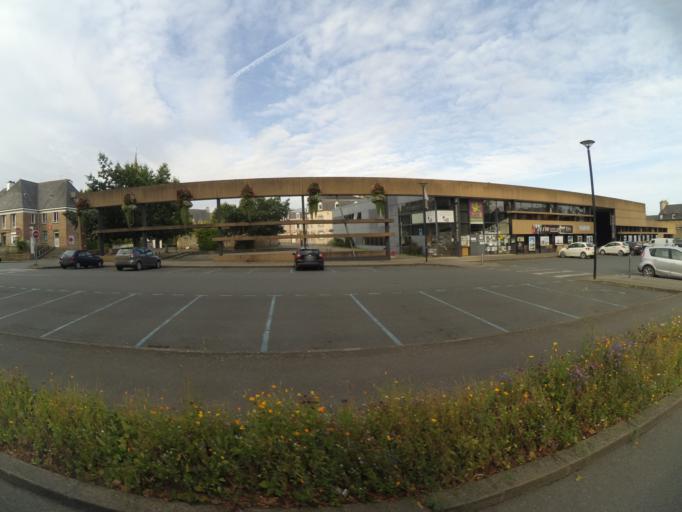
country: FR
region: Brittany
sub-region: Departement des Cotes-d'Armor
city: Guingamp
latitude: 48.5625
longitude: -3.1493
